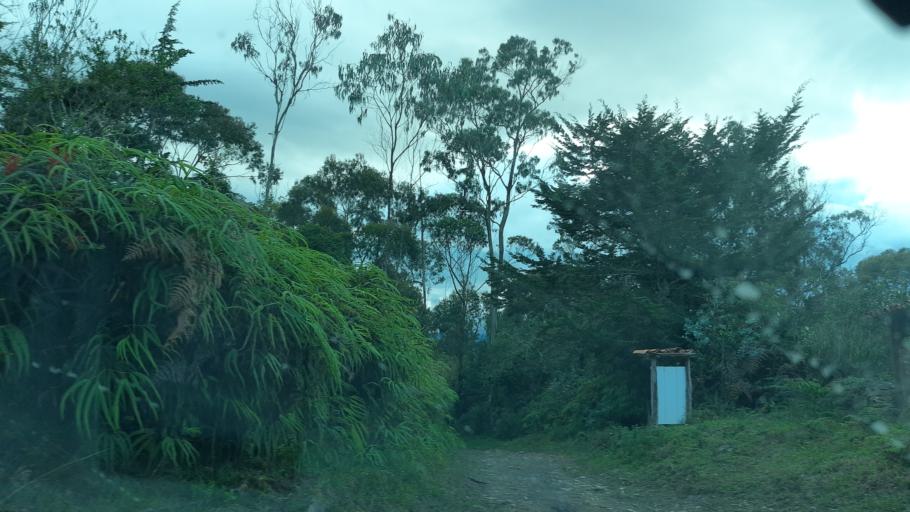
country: CO
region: Boyaca
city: Garagoa
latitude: 5.0829
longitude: -73.3182
